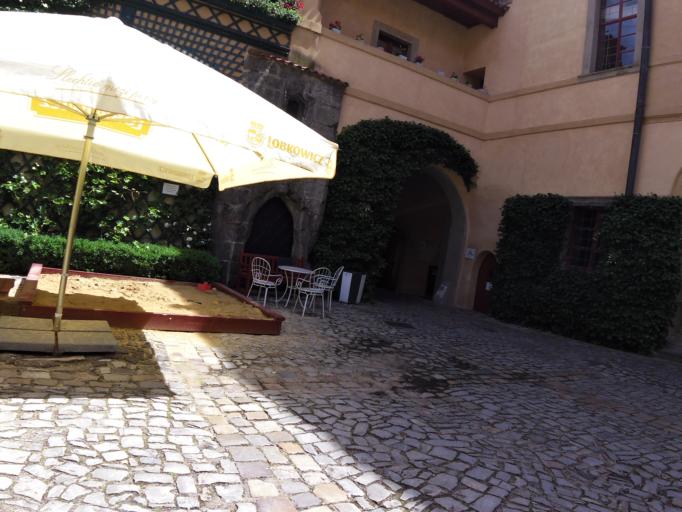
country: CZ
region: Central Bohemia
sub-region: Okres Melnik
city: Melnik
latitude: 50.3508
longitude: 14.4734
